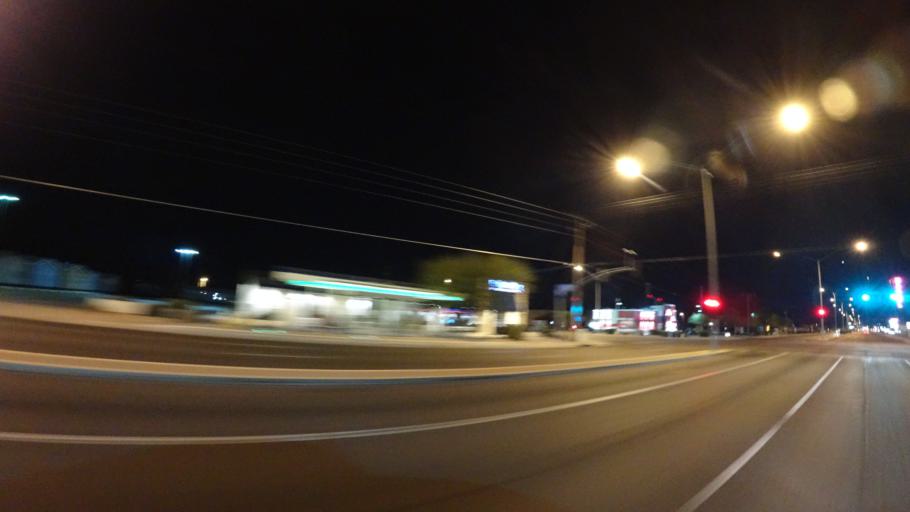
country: US
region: Arizona
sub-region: Maricopa County
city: Mesa
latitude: 33.4155
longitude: -111.7704
